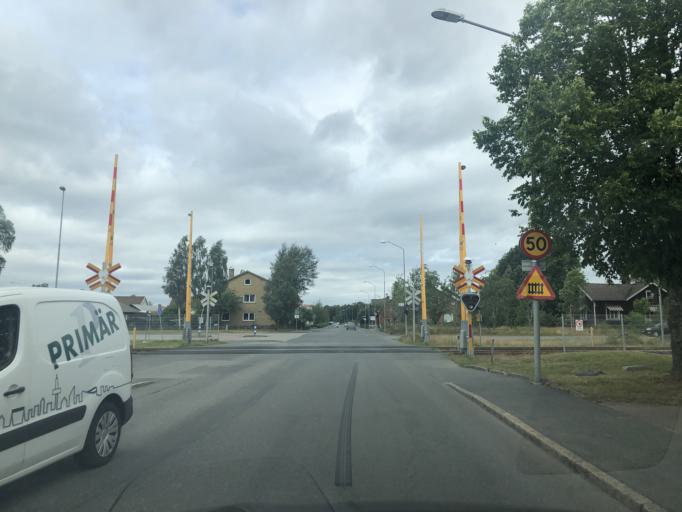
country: SE
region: Joenkoeping
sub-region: Vaggeryds Kommun
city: Vaggeryd
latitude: 57.4993
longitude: 14.1484
